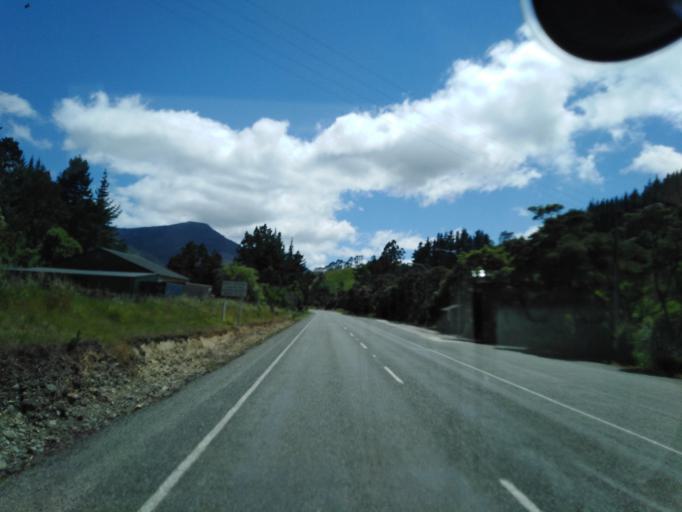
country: NZ
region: Nelson
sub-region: Nelson City
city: Nelson
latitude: -41.2226
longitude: 173.3971
